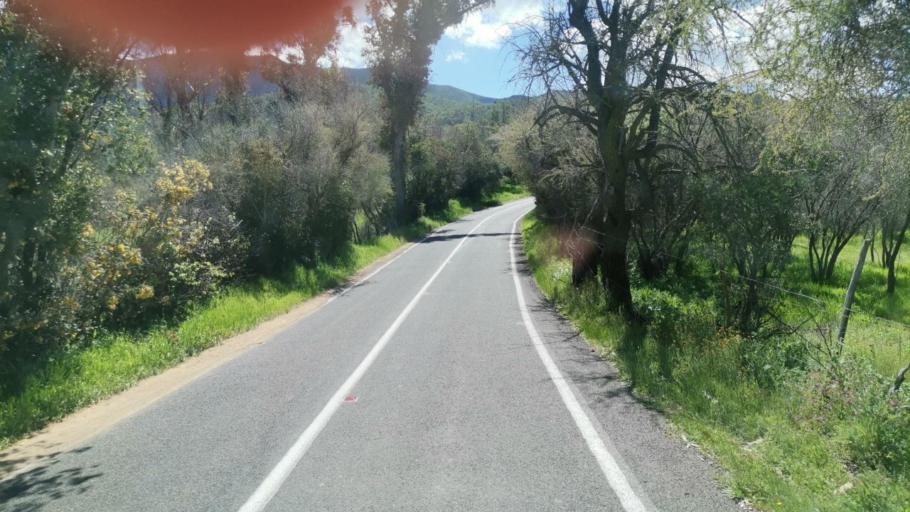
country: CL
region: Valparaiso
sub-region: Provincia de Marga Marga
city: Limache
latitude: -33.1877
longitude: -71.1916
